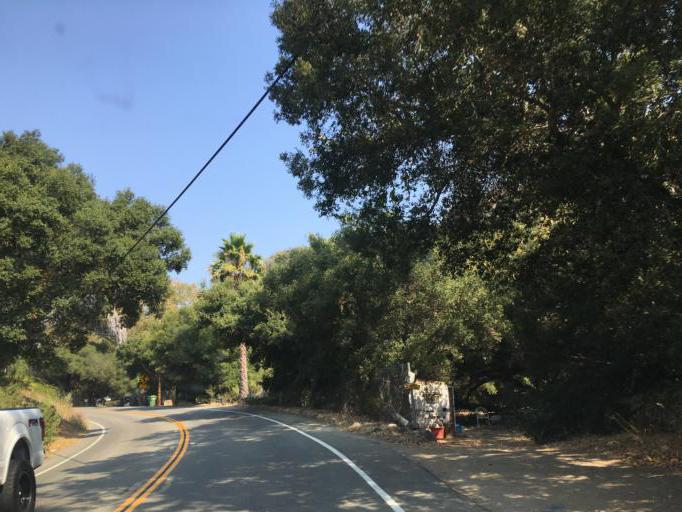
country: US
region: California
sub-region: Los Angeles County
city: Topanga
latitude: 34.0917
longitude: -118.6063
